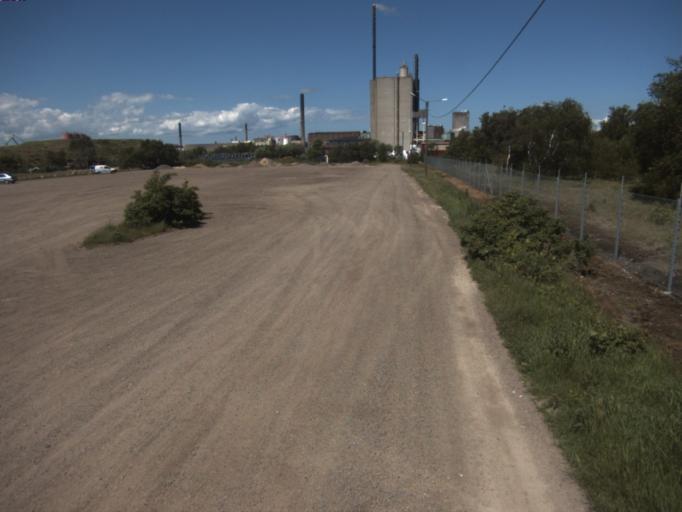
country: SE
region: Skane
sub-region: Helsingborg
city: Helsingborg
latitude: 56.0058
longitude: 12.7206
